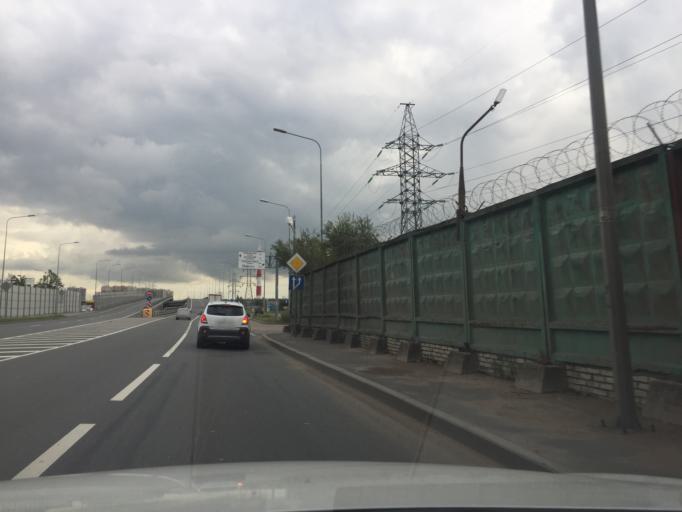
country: RU
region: St.-Petersburg
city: Dachnoye
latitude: 59.8357
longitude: 30.3054
